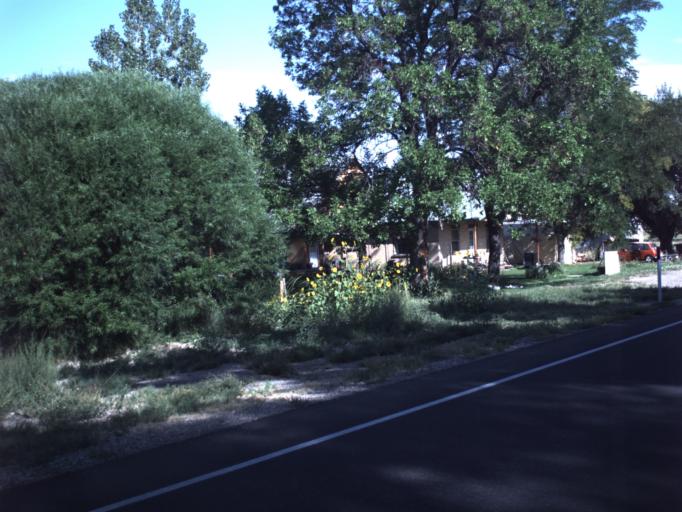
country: US
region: Utah
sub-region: Sevier County
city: Salina
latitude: 38.9972
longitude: -111.8613
